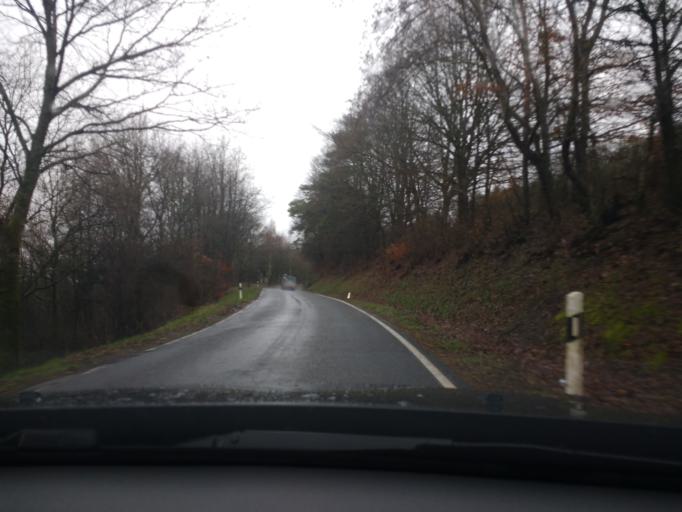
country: DE
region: Rheinland-Pfalz
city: Hinzenburg
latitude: 49.6670
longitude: 6.7262
